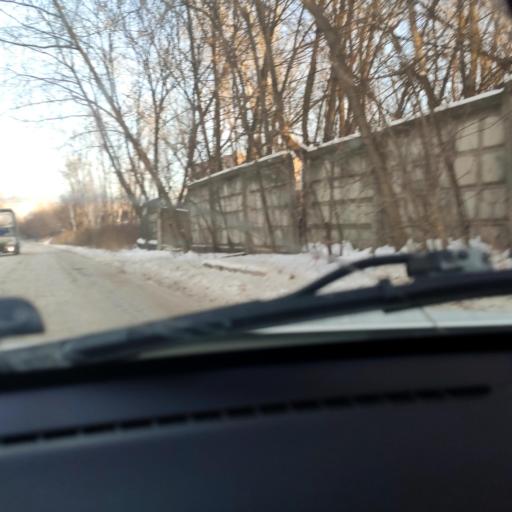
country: RU
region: Tatarstan
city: Verkhniy Uslon
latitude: 55.8009
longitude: 49.0475
